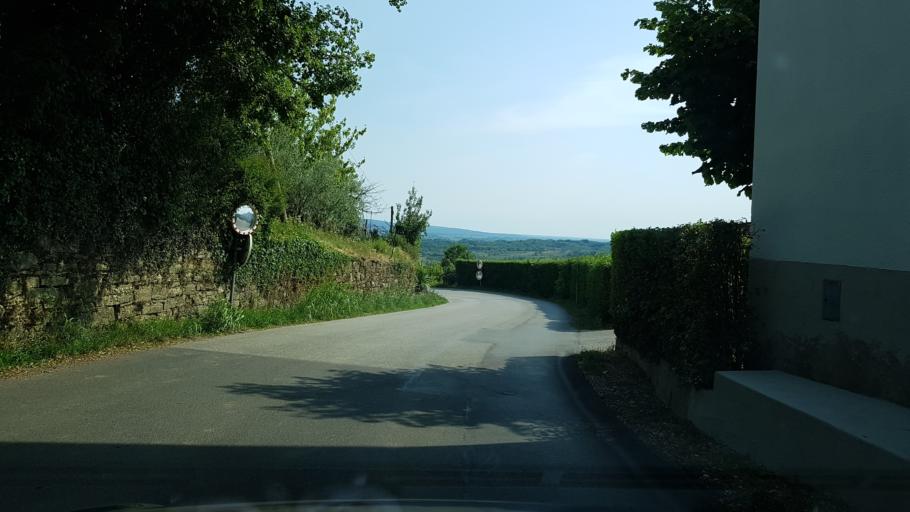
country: SI
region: Brda
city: Dobrovo
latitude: 45.9803
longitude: 13.5187
